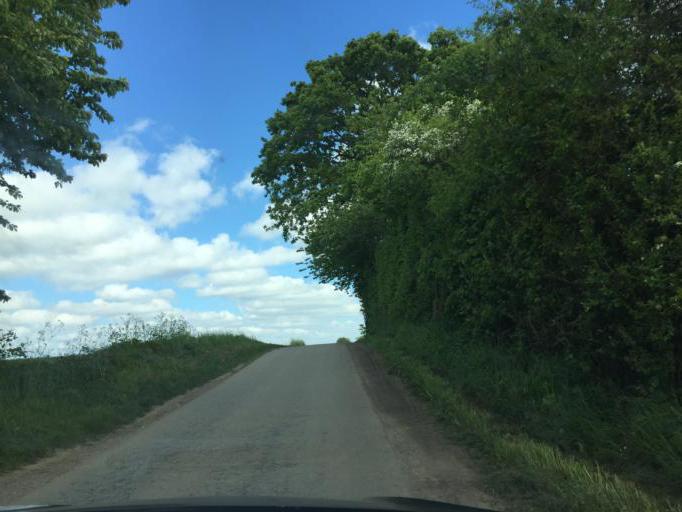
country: DK
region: South Denmark
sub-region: Assens Kommune
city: Tommerup
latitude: 55.3430
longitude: 10.2326
